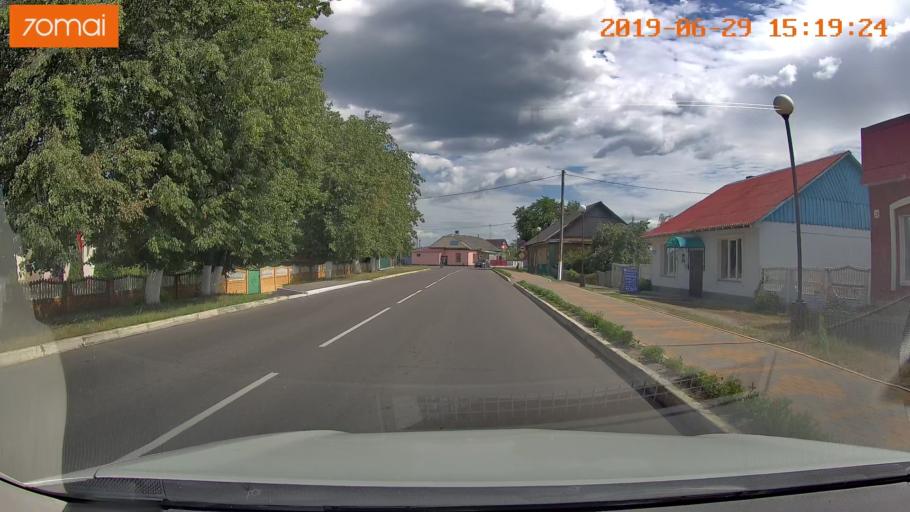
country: BY
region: Brest
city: Mikashevichy
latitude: 52.2198
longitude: 27.4689
